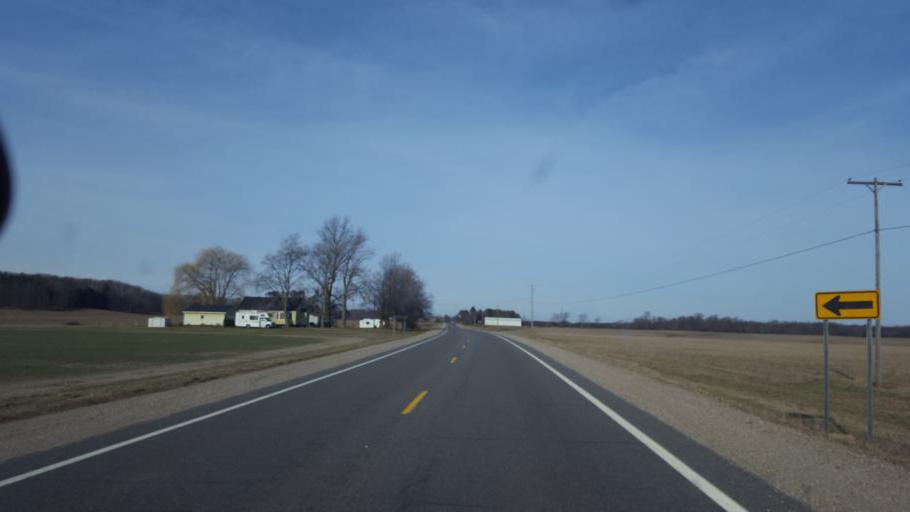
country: US
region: Michigan
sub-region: Montcalm County
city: Lakeview
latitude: 43.4329
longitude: -85.3634
